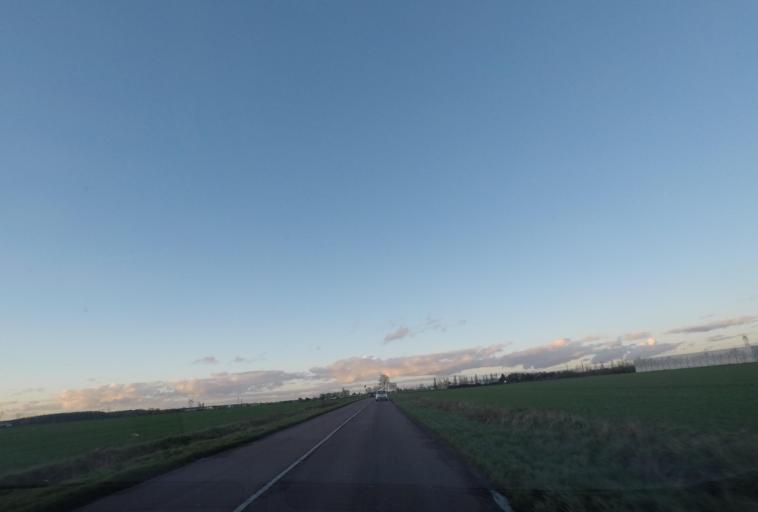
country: FR
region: Ile-de-France
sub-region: Departement de l'Essonne
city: Lisses
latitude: 48.5857
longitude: 2.4321
